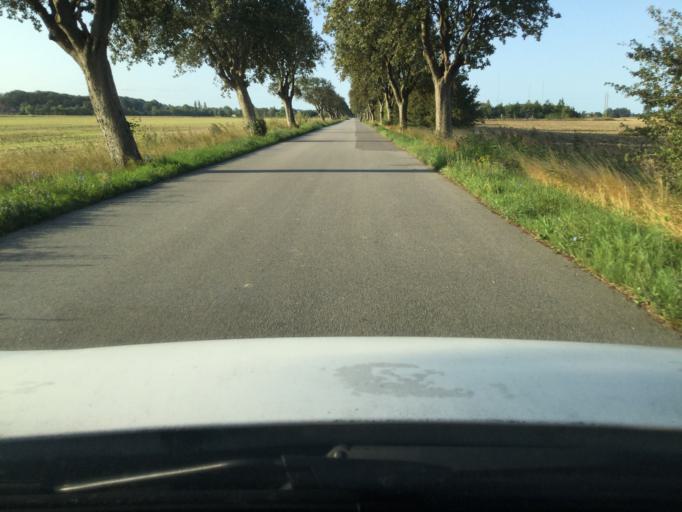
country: DK
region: Zealand
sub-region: Lolland Kommune
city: Rodby
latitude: 54.7061
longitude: 11.3885
